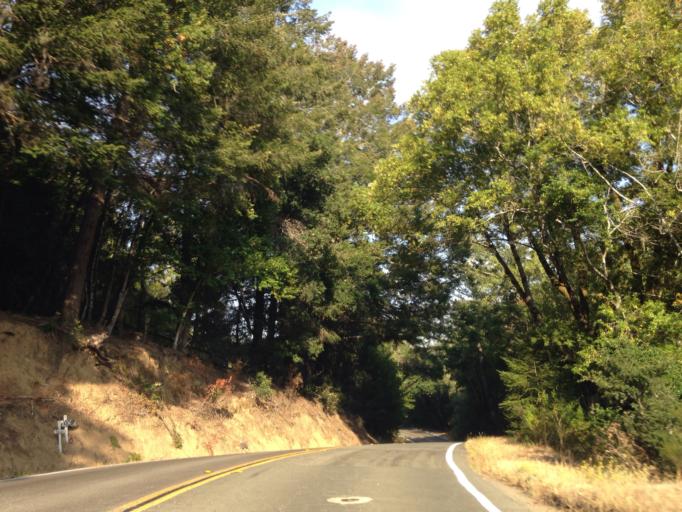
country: US
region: California
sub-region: Marin County
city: Woodacre
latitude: 38.0565
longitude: -122.6615
